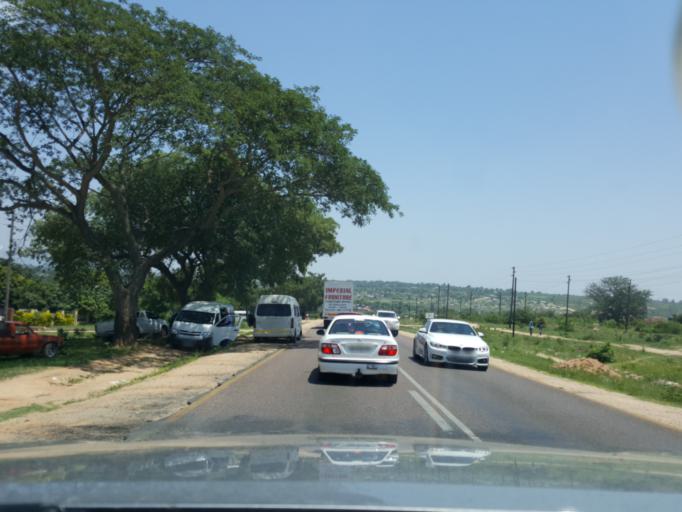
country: ZA
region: Limpopo
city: Thulamahashi
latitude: -24.7948
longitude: 31.0825
